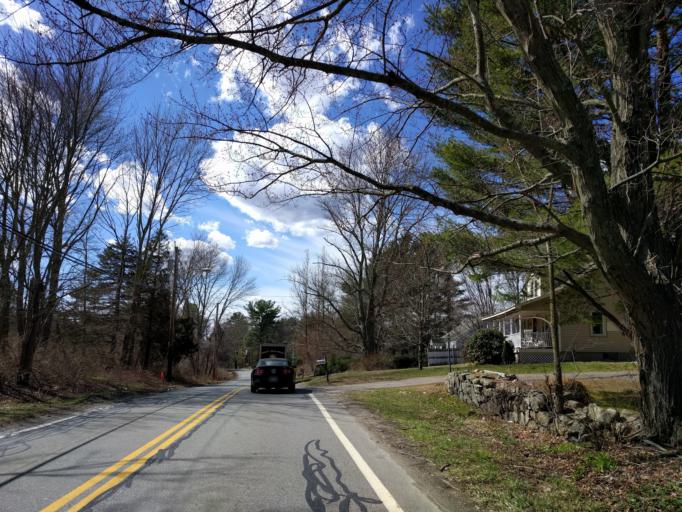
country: US
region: Massachusetts
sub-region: Norfolk County
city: Bellingham
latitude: 42.1026
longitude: -71.5069
